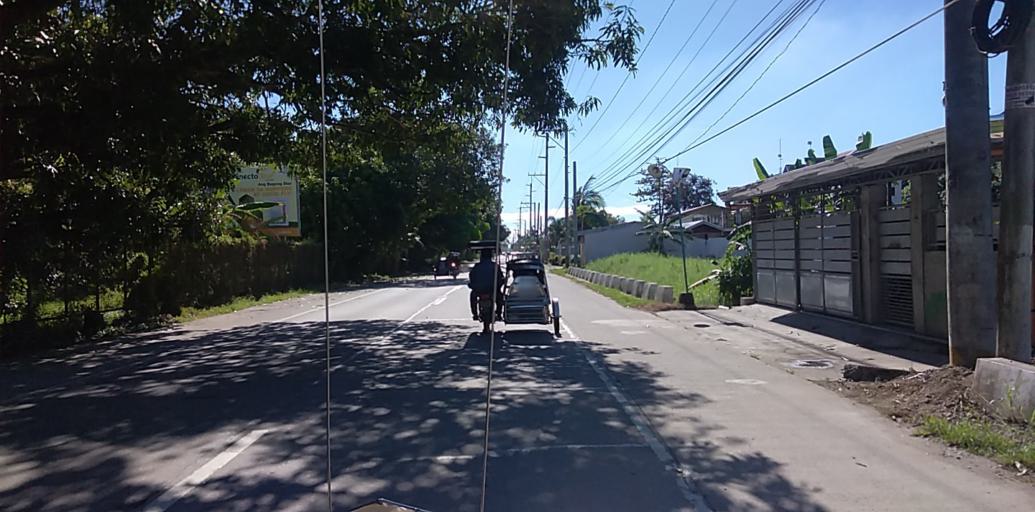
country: PH
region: Central Luzon
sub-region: Province of Pampanga
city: Santo Domingo
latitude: 15.0637
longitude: 120.7698
